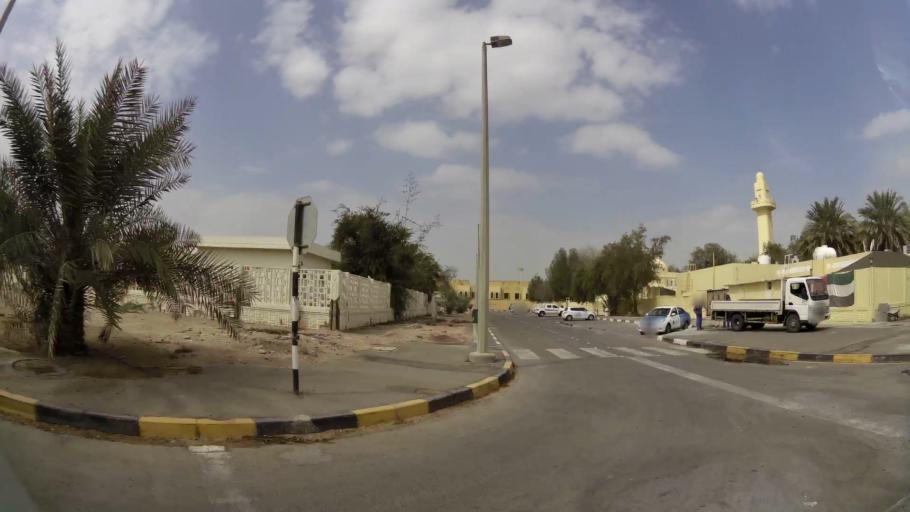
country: AE
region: Abu Dhabi
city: Abu Dhabi
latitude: 24.3963
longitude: 54.4987
